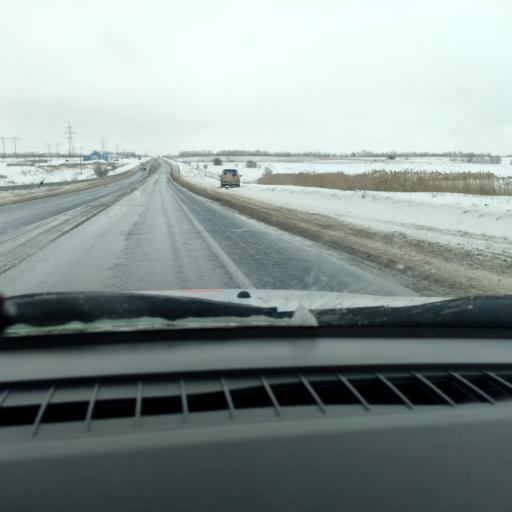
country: RU
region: Samara
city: Novokuybyshevsk
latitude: 53.0101
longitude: 50.0758
